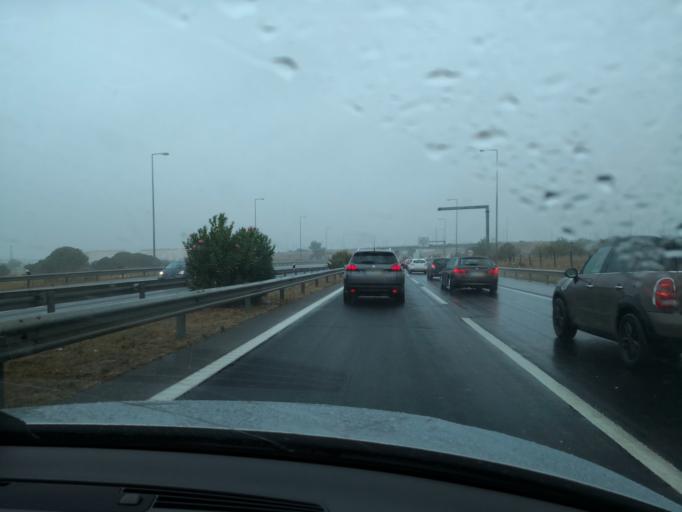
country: PT
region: Setubal
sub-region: Montijo
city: Montijo
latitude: 38.6984
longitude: -8.9402
